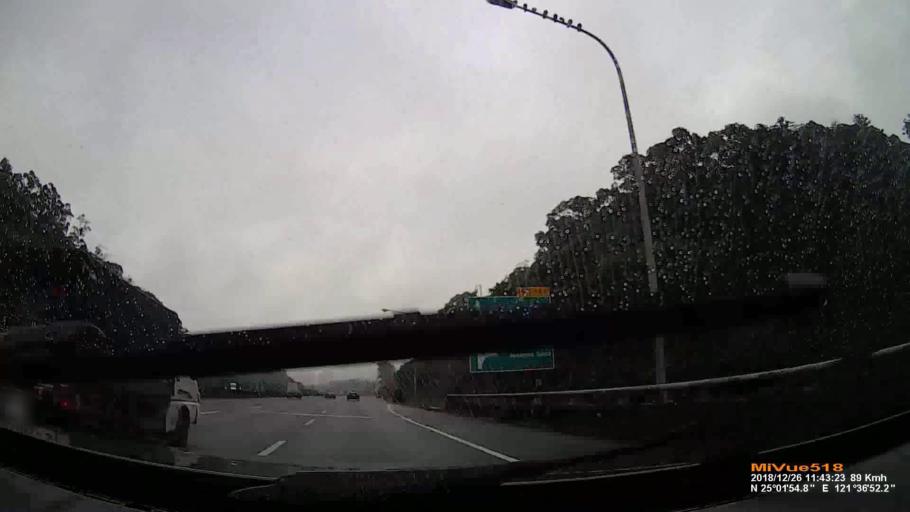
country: TW
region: Taipei
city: Taipei
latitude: 25.0347
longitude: 121.6251
